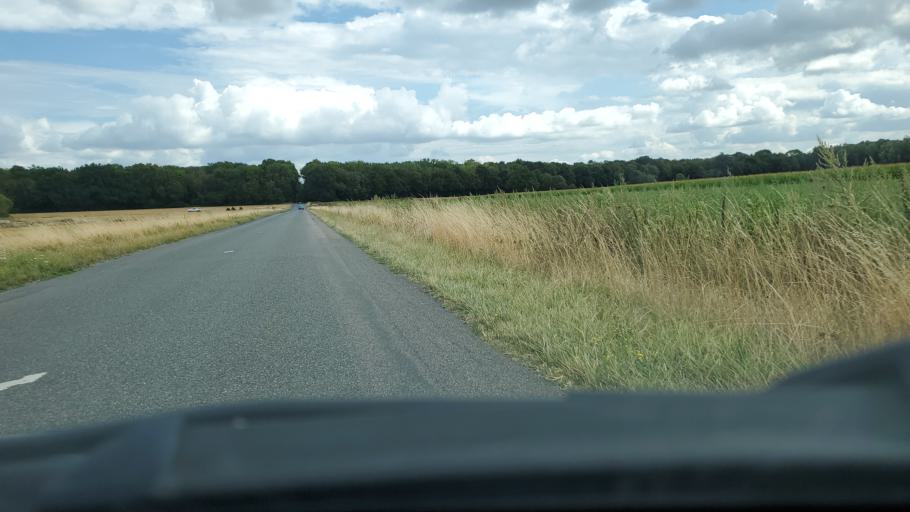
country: FR
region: Ile-de-France
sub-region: Departement de Seine-et-Marne
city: Pommeuse
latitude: 48.8623
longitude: 3.0053
